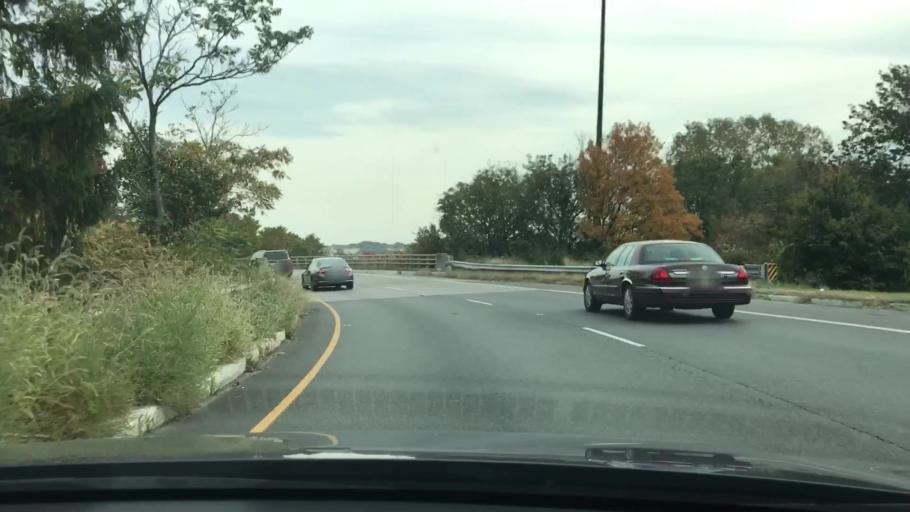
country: US
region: New Jersey
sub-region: Bergen County
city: Rutherford
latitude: 40.8096
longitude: -74.1012
